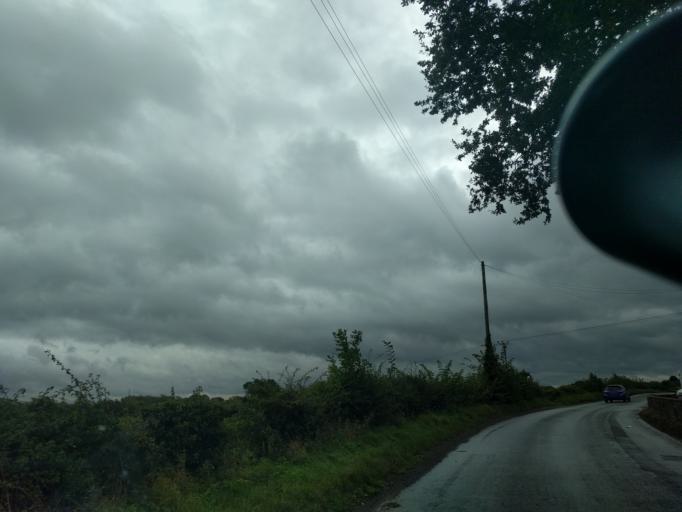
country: GB
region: England
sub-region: North Yorkshire
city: Bedale
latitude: 54.3292
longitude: -1.5678
